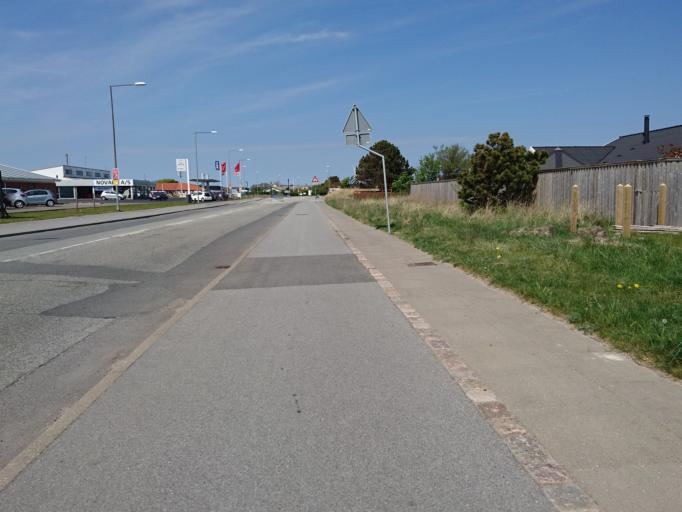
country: DK
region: North Denmark
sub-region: Frederikshavn Kommune
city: Skagen
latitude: 57.7254
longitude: 10.5704
